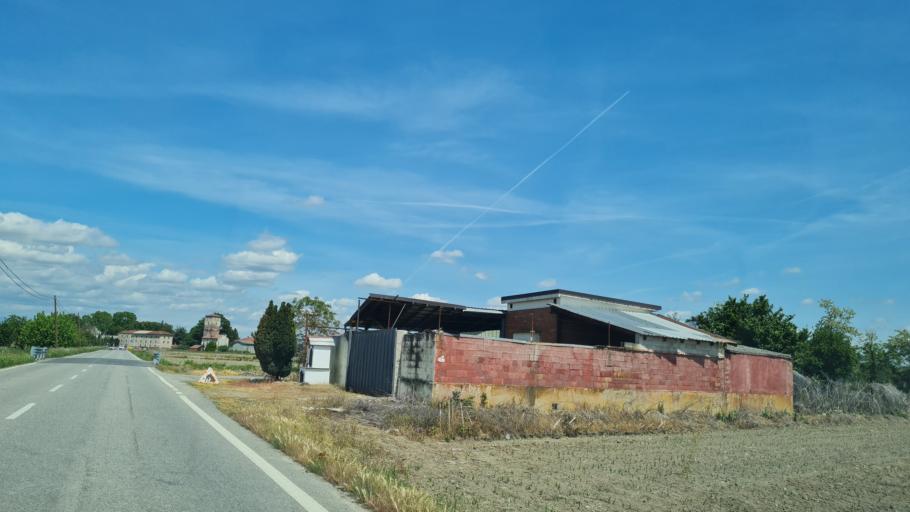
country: IT
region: Piedmont
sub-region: Provincia di Novara
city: Mandello Vitta
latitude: 45.4894
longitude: 8.4587
